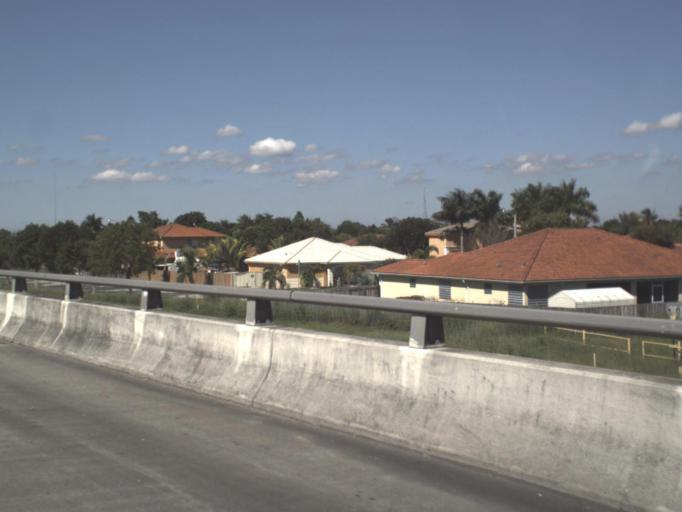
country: US
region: Florida
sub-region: Miami-Dade County
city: Princeton
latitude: 25.5296
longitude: -80.3881
